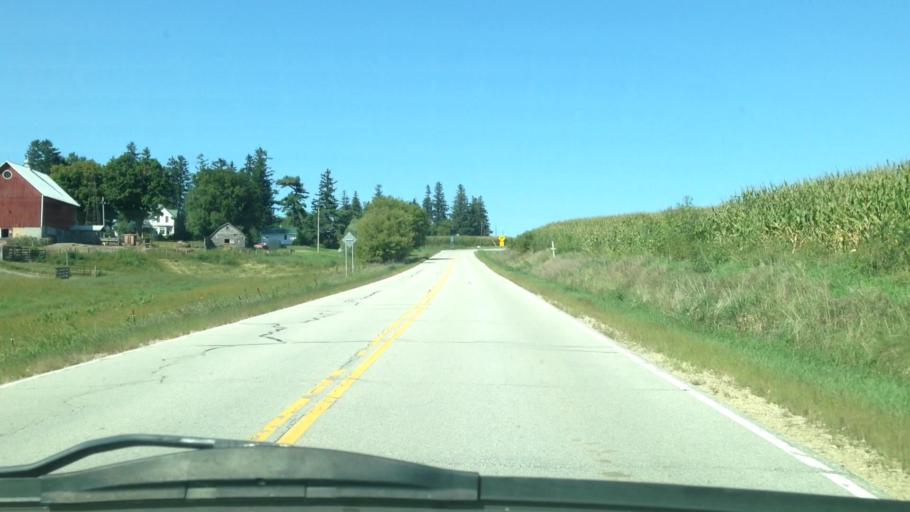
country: US
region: Minnesota
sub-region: Fillmore County
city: Rushford
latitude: 43.6892
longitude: -91.7753
